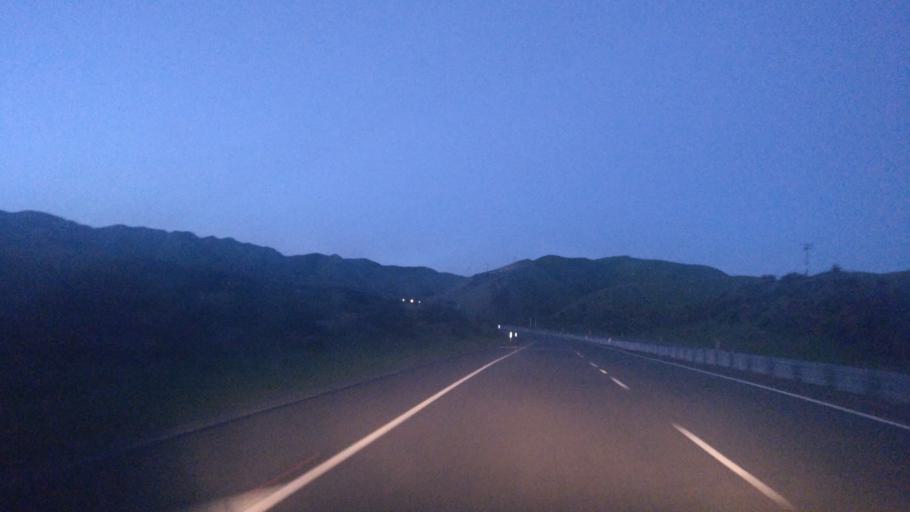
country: NZ
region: Wellington
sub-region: Porirua City
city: Porirua
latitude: -41.0663
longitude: 174.8771
